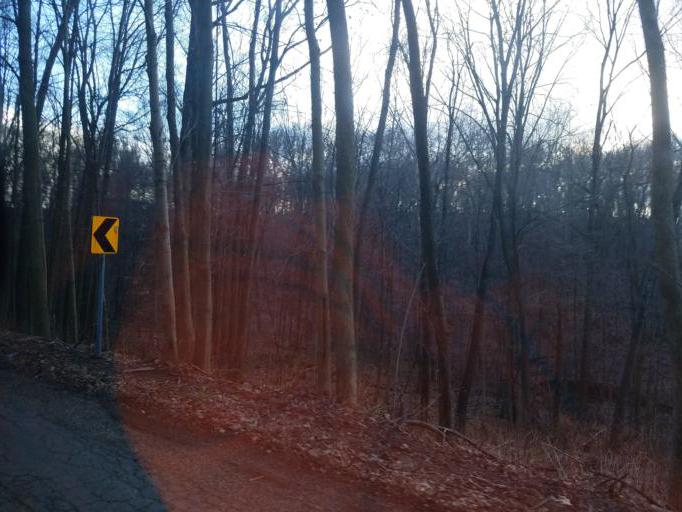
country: US
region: Ohio
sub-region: Sandusky County
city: Bellville
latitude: 40.6266
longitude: -82.3792
